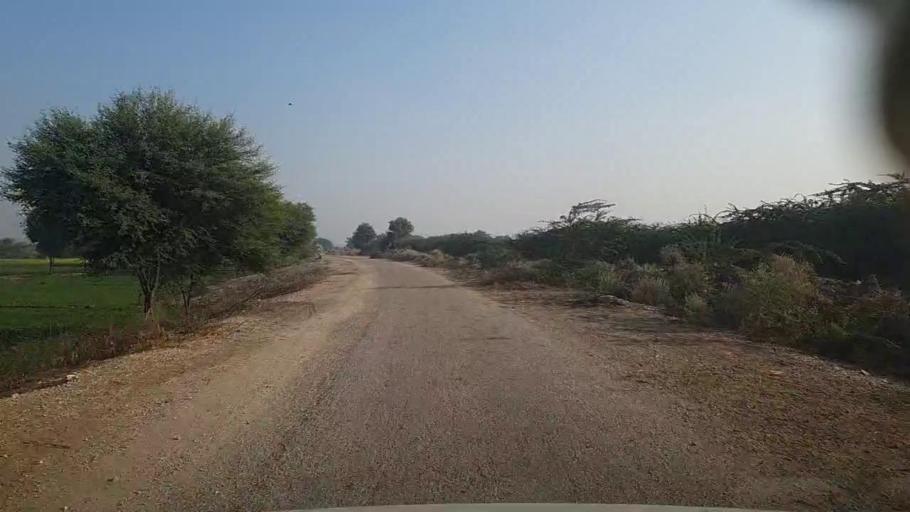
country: PK
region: Sindh
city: Karaundi
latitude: 26.7407
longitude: 68.4780
